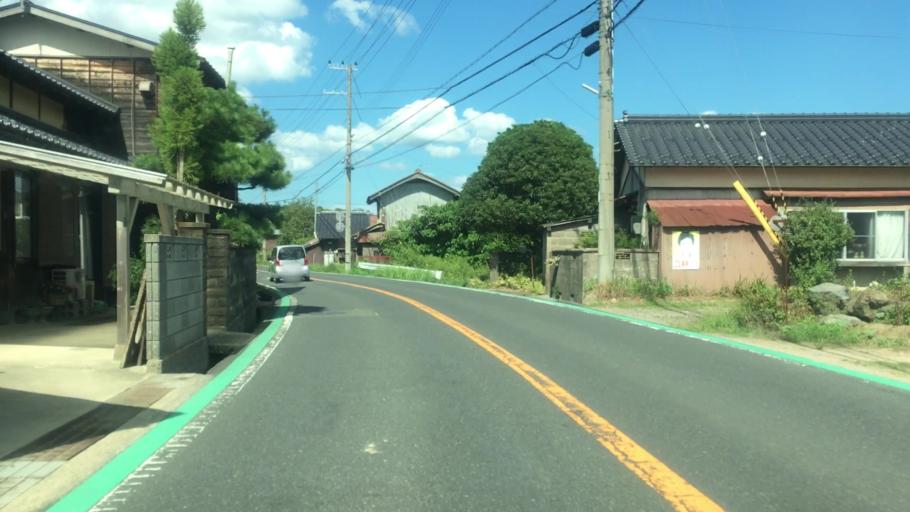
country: JP
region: Kyoto
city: Miyazu
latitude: 35.6098
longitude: 135.0528
